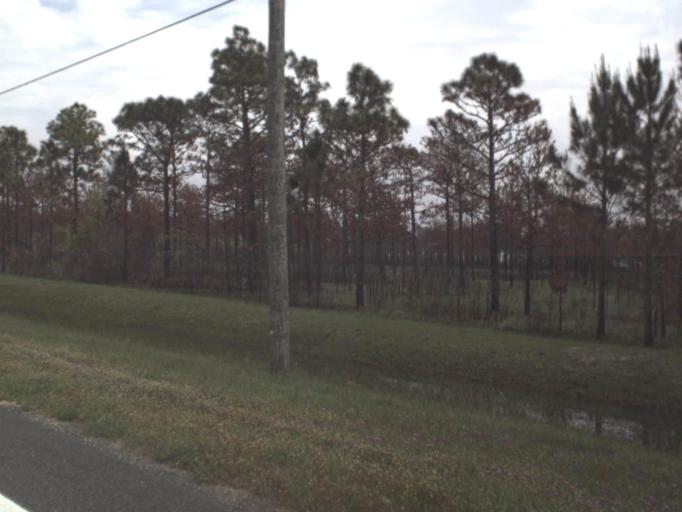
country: US
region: Florida
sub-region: Santa Rosa County
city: Oriole Beach
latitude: 30.4617
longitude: -87.0916
